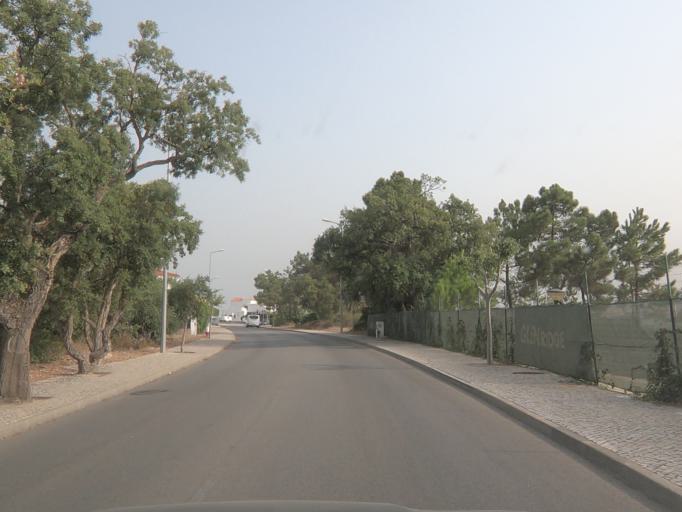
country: PT
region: Faro
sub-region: Albufeira
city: Guia
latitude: 37.0877
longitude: -8.3101
